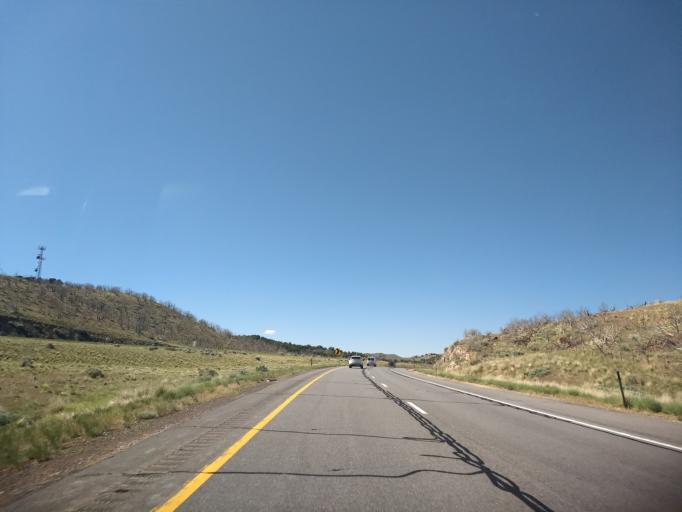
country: US
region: Utah
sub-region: Beaver County
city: Beaver
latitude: 38.6327
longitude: -112.6090
